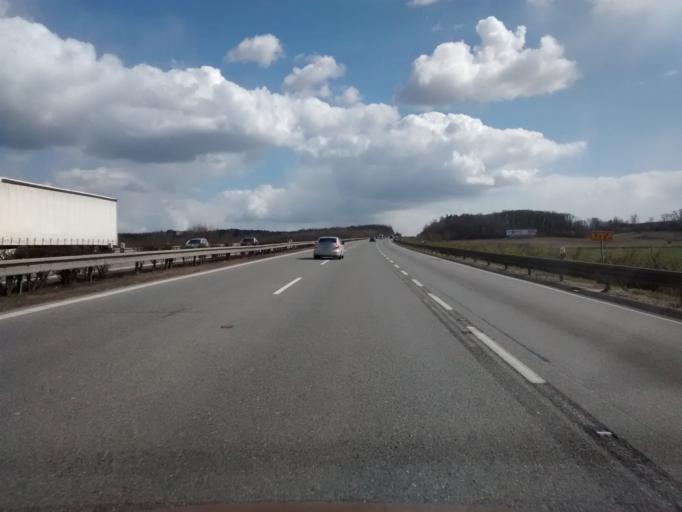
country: CZ
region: Central Bohemia
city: Odolena Voda
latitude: 50.2360
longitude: 14.3909
